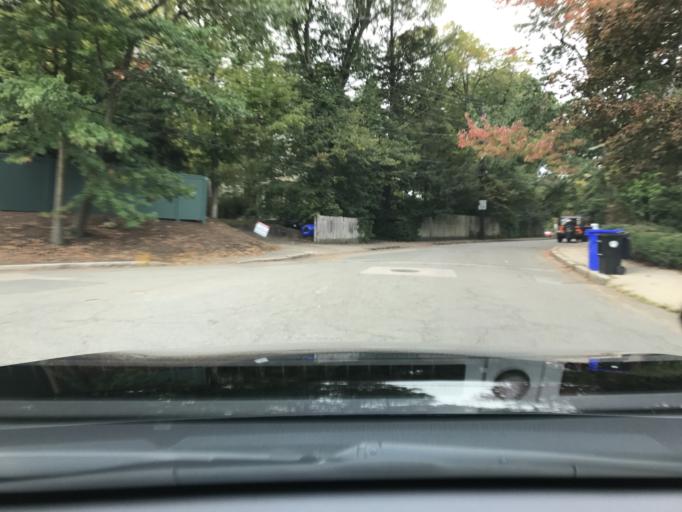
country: US
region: Massachusetts
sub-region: Norfolk County
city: Brookline
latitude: 42.3266
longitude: -71.1264
